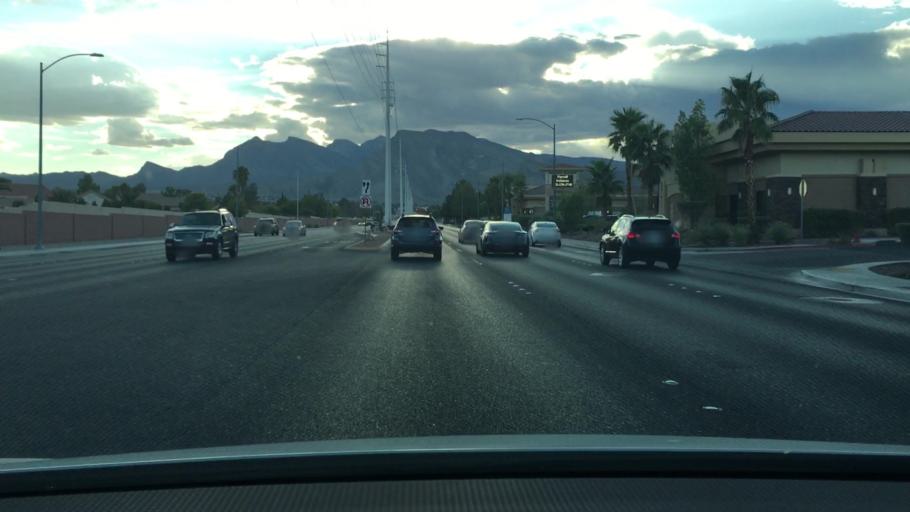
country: US
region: Nevada
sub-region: Clark County
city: Summerlin South
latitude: 36.2185
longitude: -115.2833
